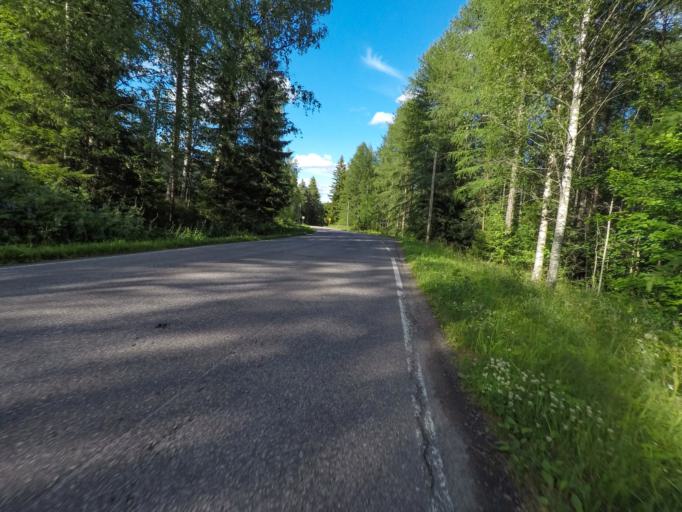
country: FI
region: South Karelia
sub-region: Imatra
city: Imatra
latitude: 61.1426
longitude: 28.7440
